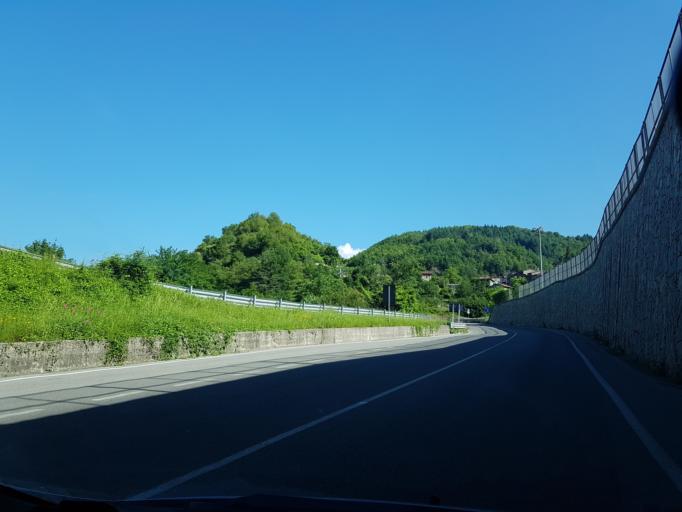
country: IT
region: Tuscany
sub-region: Provincia di Lucca
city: Piazza al Serchio-San Michele
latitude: 44.1791
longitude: 10.3101
